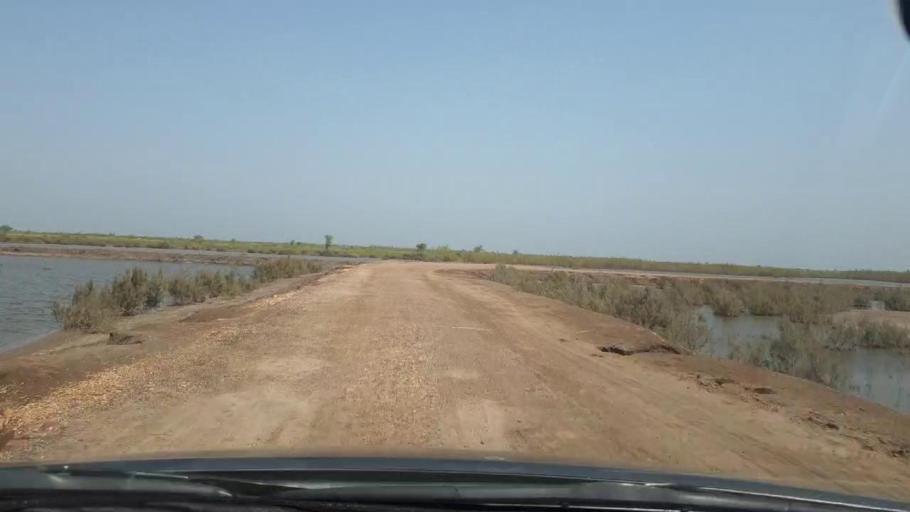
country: PK
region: Sindh
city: Tando Bago
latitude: 24.7913
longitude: 69.0787
